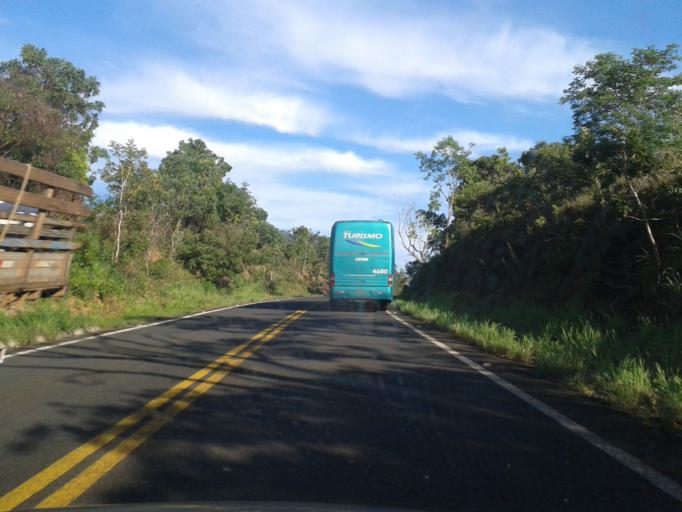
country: BR
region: Minas Gerais
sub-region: Tupaciguara
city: Tupaciguara
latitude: -18.3032
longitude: -48.5622
